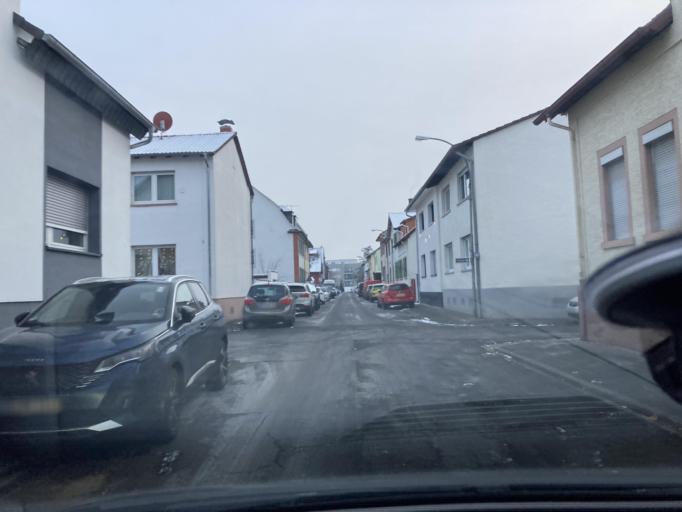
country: DE
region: Hesse
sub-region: Regierungsbezirk Darmstadt
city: Muehlheim am Main
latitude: 50.1216
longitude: 8.8343
